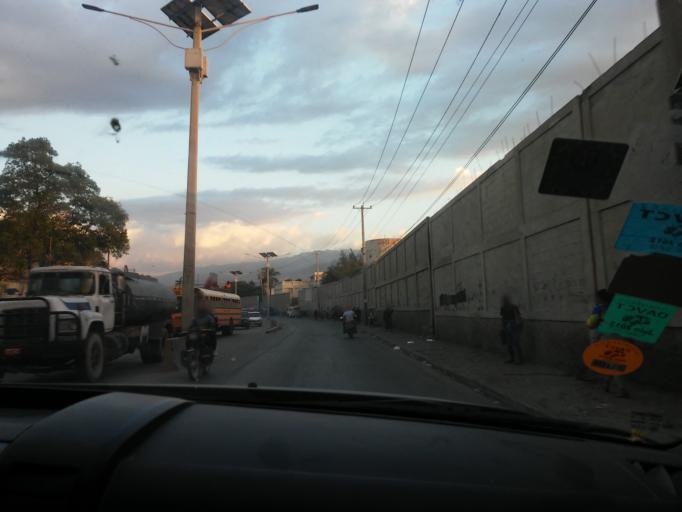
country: HT
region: Ouest
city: Port-au-Prince
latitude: 18.5620
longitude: -72.3405
